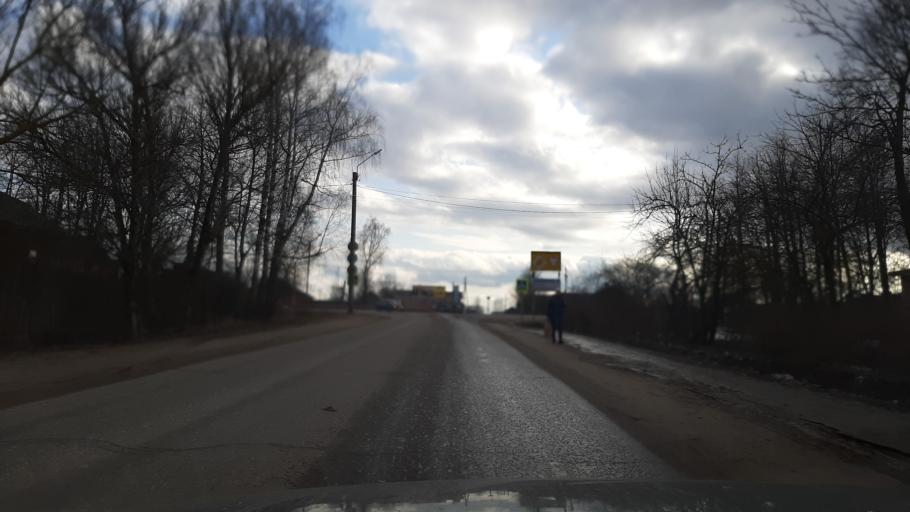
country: RU
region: Ivanovo
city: Teykovo
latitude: 56.8559
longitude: 40.5192
